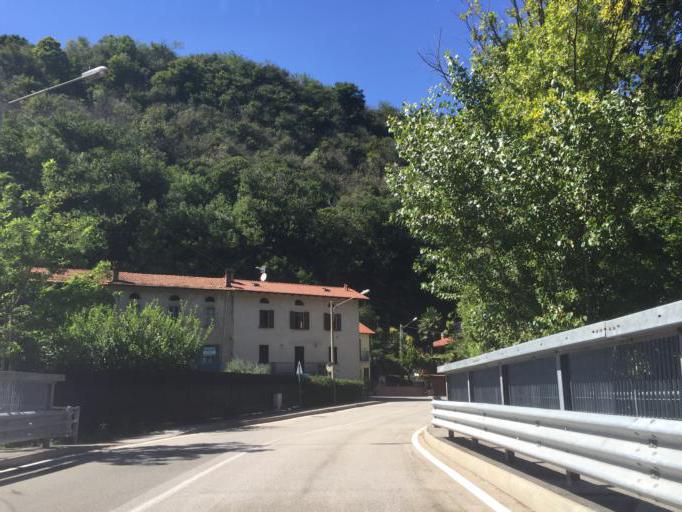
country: IT
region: Lombardy
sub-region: Provincia di Varese
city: Porto Ceresio
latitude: 45.9061
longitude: 8.8959
